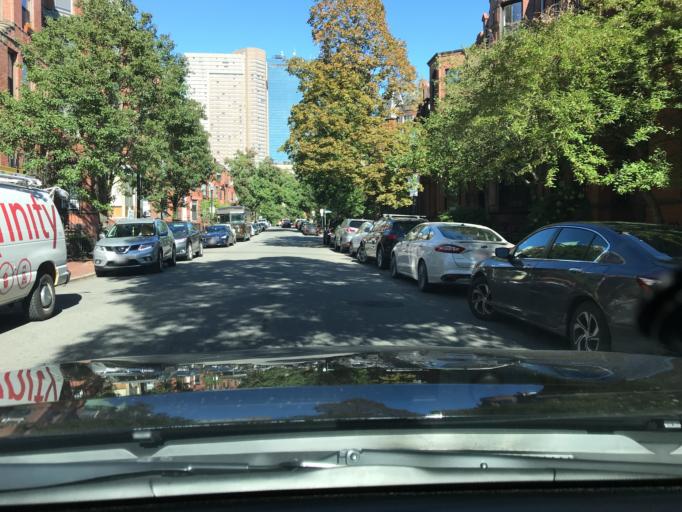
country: US
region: Massachusetts
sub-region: Suffolk County
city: Boston
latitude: 42.3438
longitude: -71.0821
